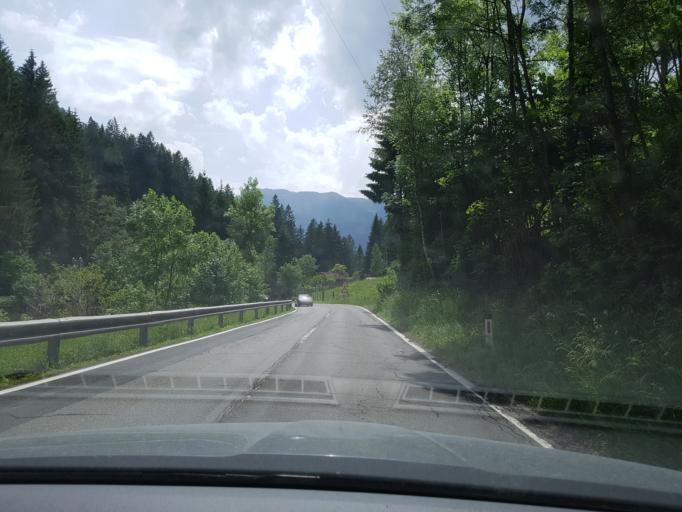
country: AT
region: Carinthia
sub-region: Politischer Bezirk Villach Land
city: Feld am See
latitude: 46.8055
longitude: 13.7602
